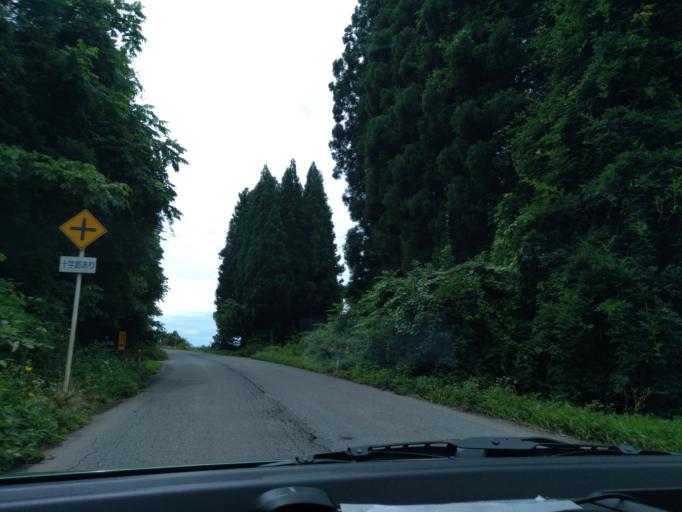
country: JP
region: Akita
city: Kakunodatemachi
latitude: 39.5887
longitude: 140.6191
